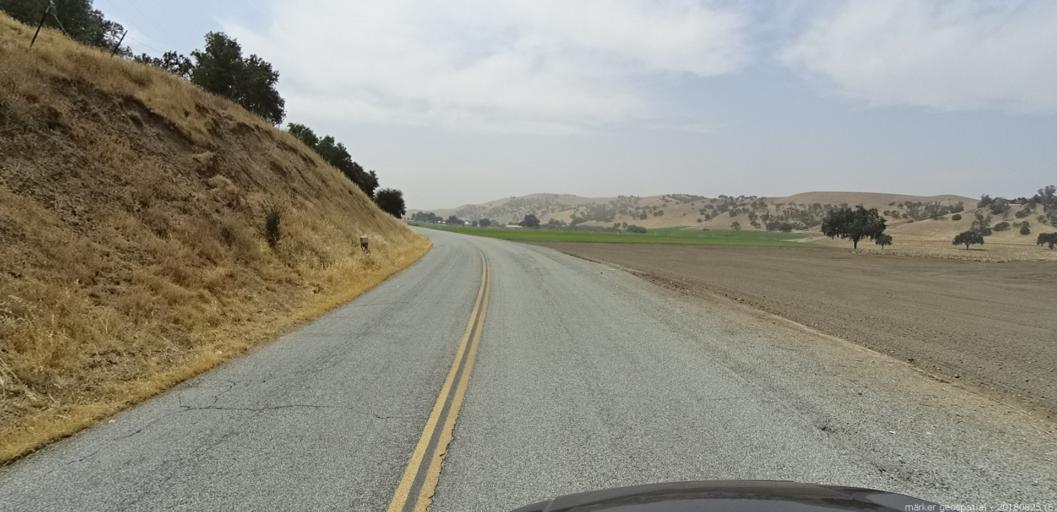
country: US
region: California
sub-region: San Luis Obispo County
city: San Miguel
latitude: 35.8171
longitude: -120.6627
